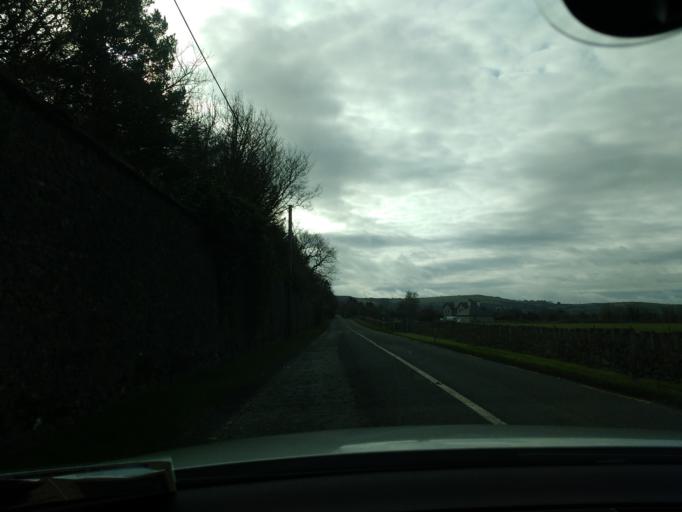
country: IE
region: Leinster
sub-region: Laois
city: Rathdowney
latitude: 52.6706
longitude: -7.5815
